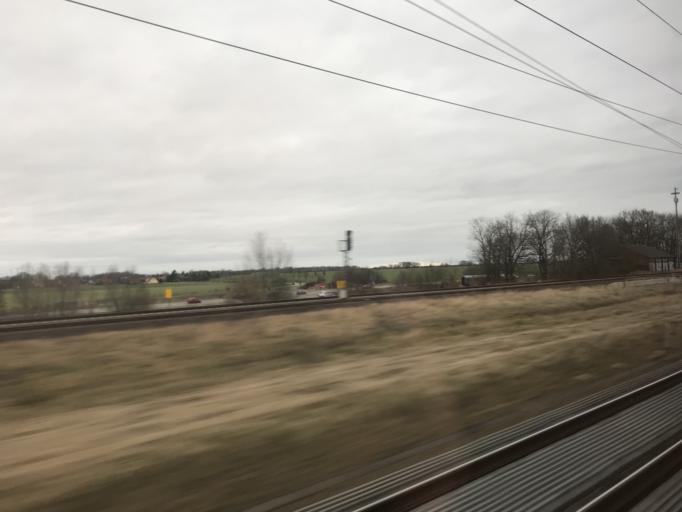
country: DE
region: Saxony-Anhalt
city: Uchtspringe
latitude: 52.5664
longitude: 11.6607
